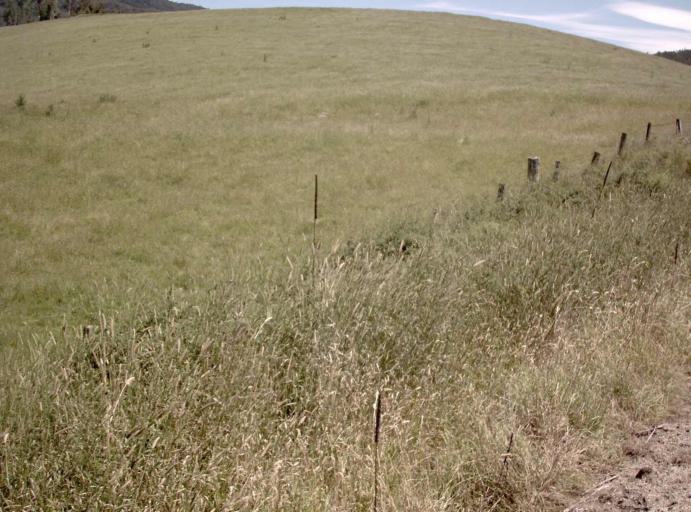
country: AU
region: Victoria
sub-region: East Gippsland
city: Lakes Entrance
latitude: -37.3951
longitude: 148.2168
